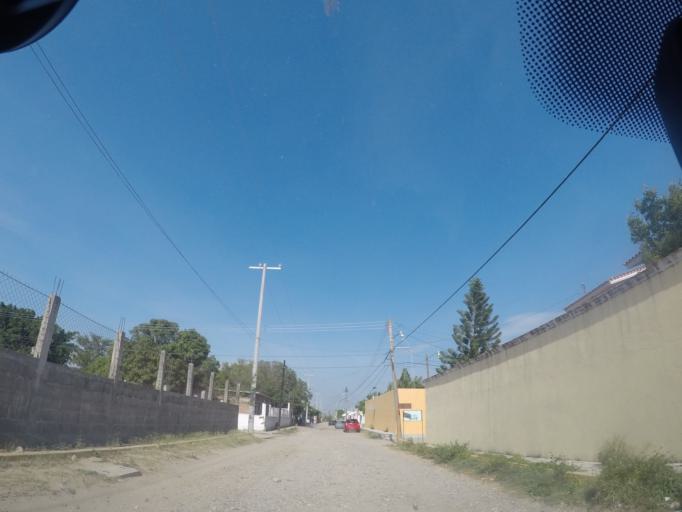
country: MX
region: Oaxaca
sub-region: Salina Cruz
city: Salina Cruz
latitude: 16.2168
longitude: -95.1946
